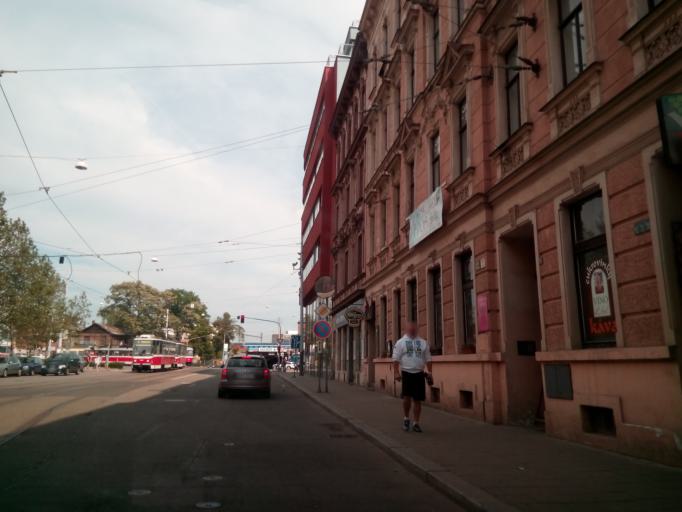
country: CZ
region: South Moravian
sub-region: Mesto Brno
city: Brno
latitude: 49.1892
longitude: 16.6062
